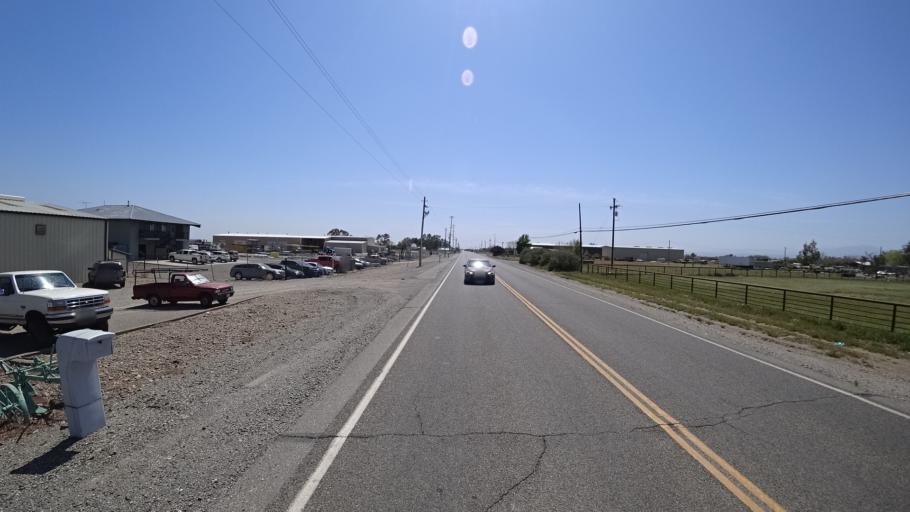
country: US
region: California
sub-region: Glenn County
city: Orland
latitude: 39.6921
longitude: -122.1966
